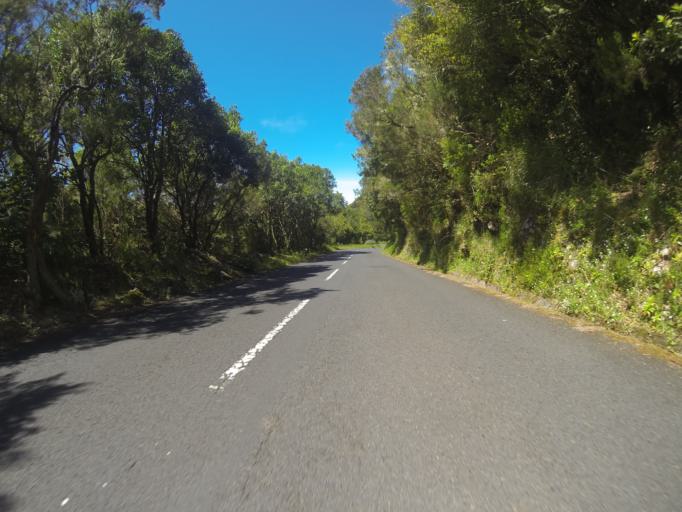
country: PT
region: Madeira
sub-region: Santana
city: Santana
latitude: 32.7343
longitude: -16.8849
